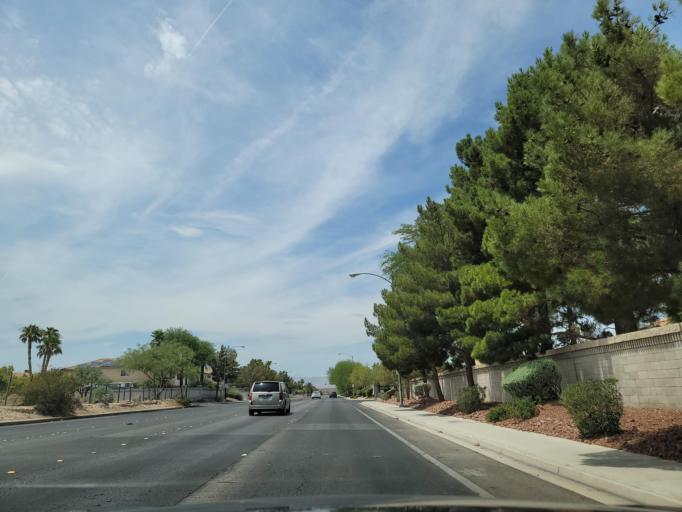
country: US
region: Nevada
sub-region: Clark County
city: Whitney
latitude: 36.0207
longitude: -115.1421
